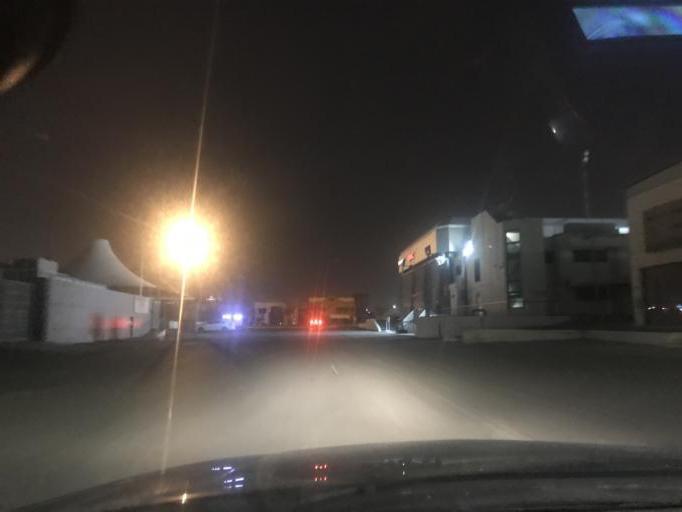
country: SA
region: Ar Riyad
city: Riyadh
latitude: 24.7257
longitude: 46.7824
